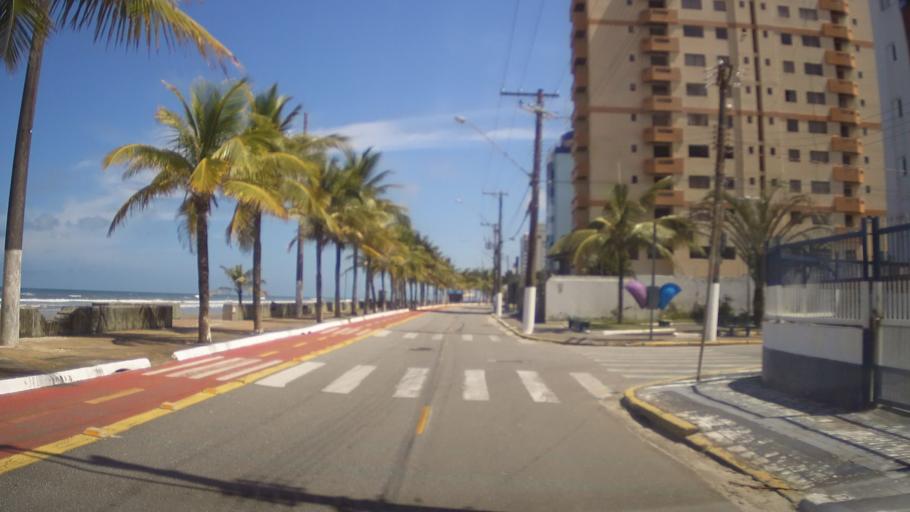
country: BR
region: Sao Paulo
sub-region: Mongagua
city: Mongagua
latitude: -24.0906
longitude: -46.6088
